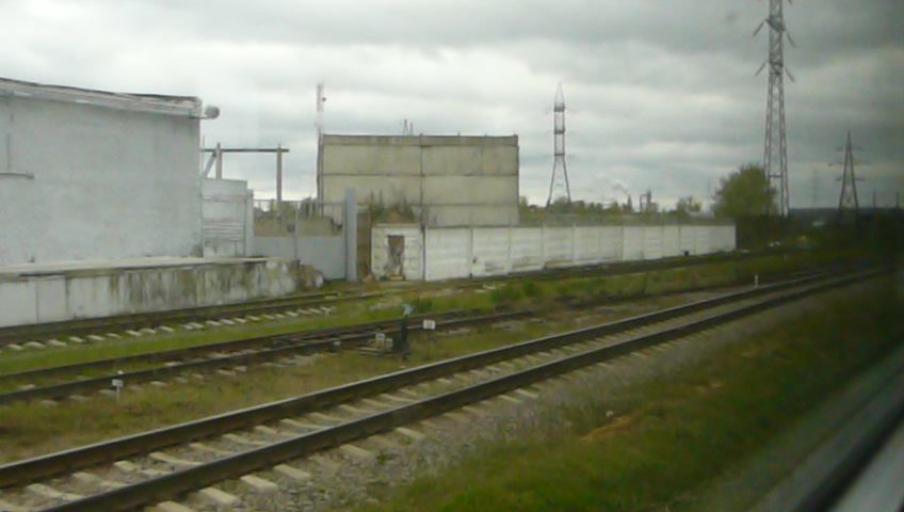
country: RU
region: Moskovskaya
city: Yegor'yevsk
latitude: 55.3956
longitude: 39.0045
